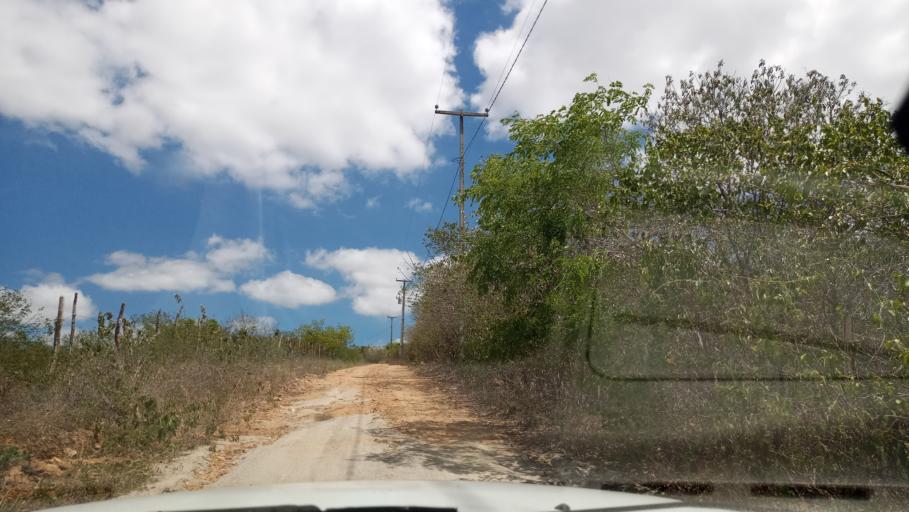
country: BR
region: Rio Grande do Norte
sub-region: Sao Paulo Do Potengi
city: Sao Paulo do Potengi
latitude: -5.7477
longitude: -35.9102
